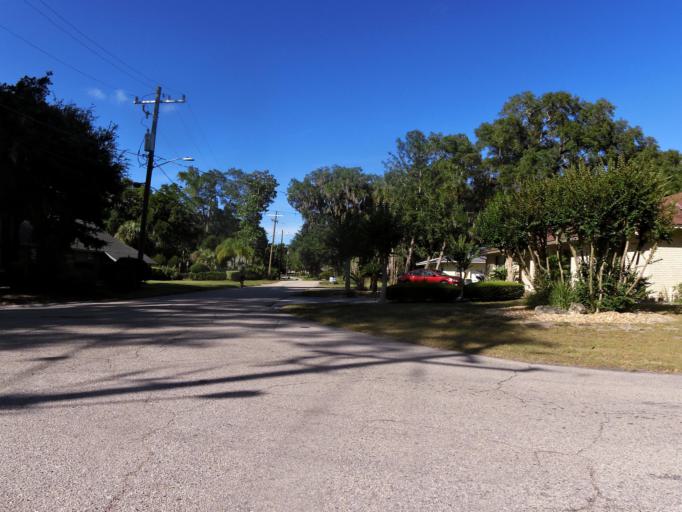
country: US
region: Florida
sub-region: Duval County
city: Jacksonville
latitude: 30.3136
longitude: -81.6179
